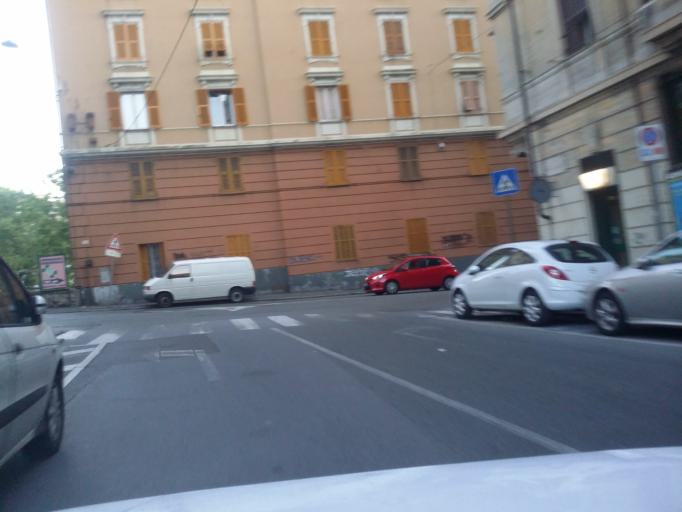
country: IT
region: Liguria
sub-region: Provincia di Genova
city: Genoa
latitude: 44.4074
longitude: 8.9639
